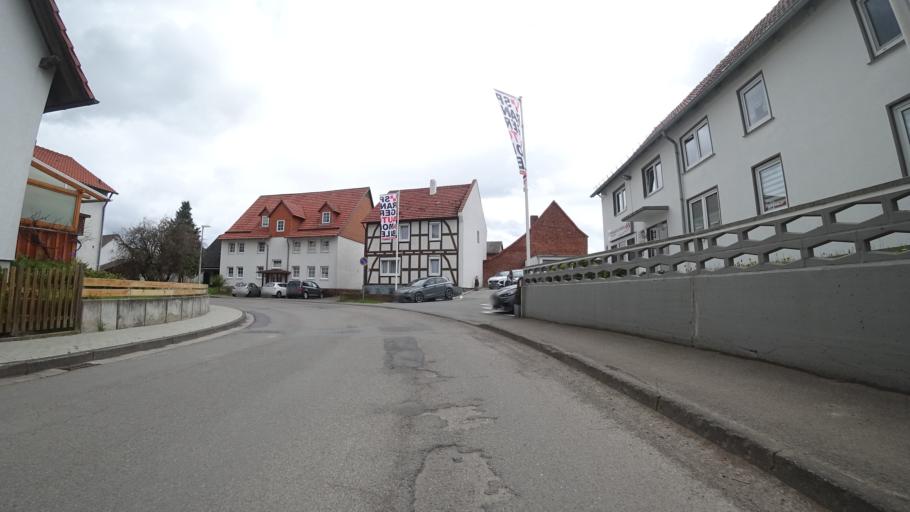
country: DE
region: Hesse
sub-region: Regierungsbezirk Kassel
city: Zierenberg
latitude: 51.4346
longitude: 9.3280
